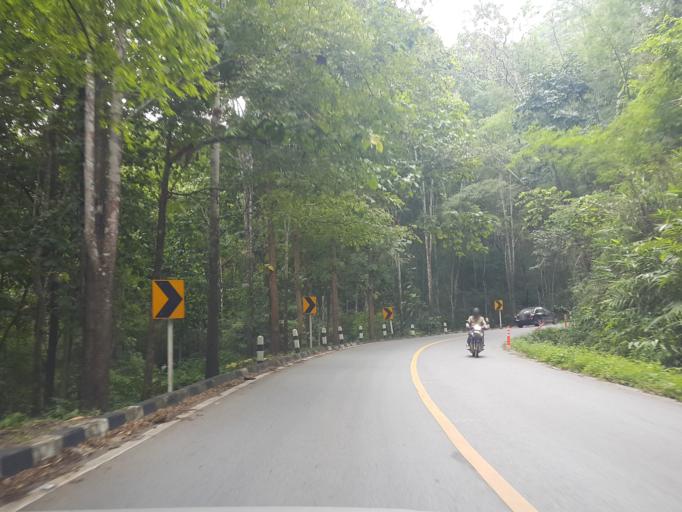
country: TH
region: Mae Hong Son
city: Mae Hi
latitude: 19.2729
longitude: 98.4996
